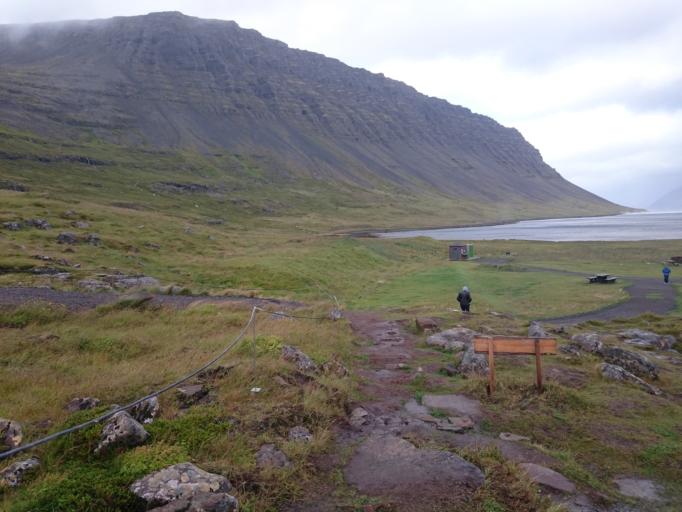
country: IS
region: Westfjords
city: Isafjoerdur
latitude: 65.7360
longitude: -23.2074
